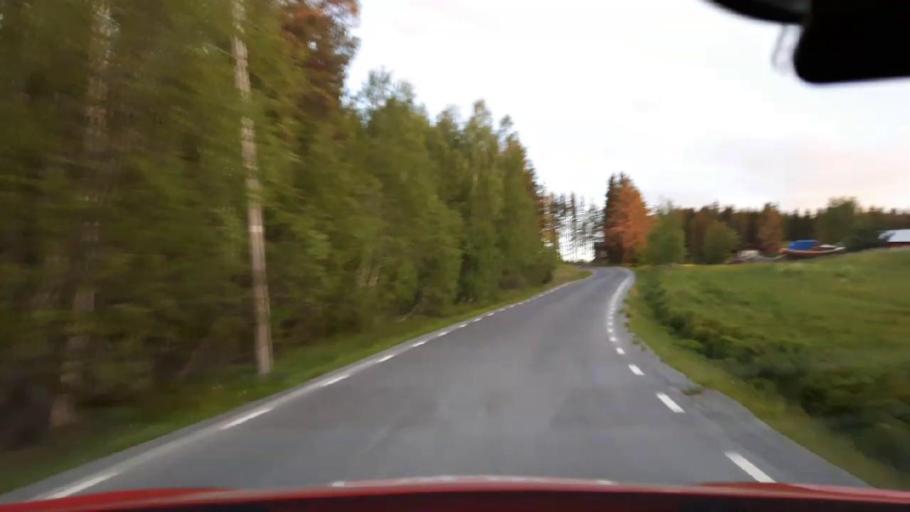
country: SE
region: Jaemtland
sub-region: OEstersunds Kommun
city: Brunflo
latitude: 63.0661
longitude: 14.8055
